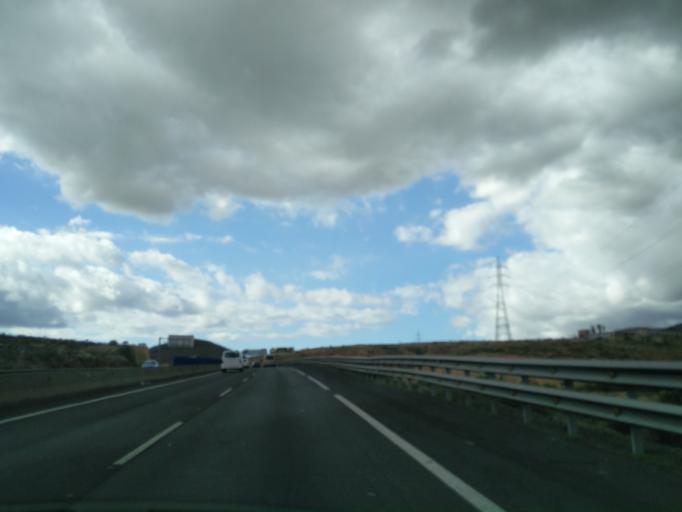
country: ES
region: Canary Islands
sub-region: Provincia de Santa Cruz de Tenerife
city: Arona
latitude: 28.0577
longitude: -16.6862
